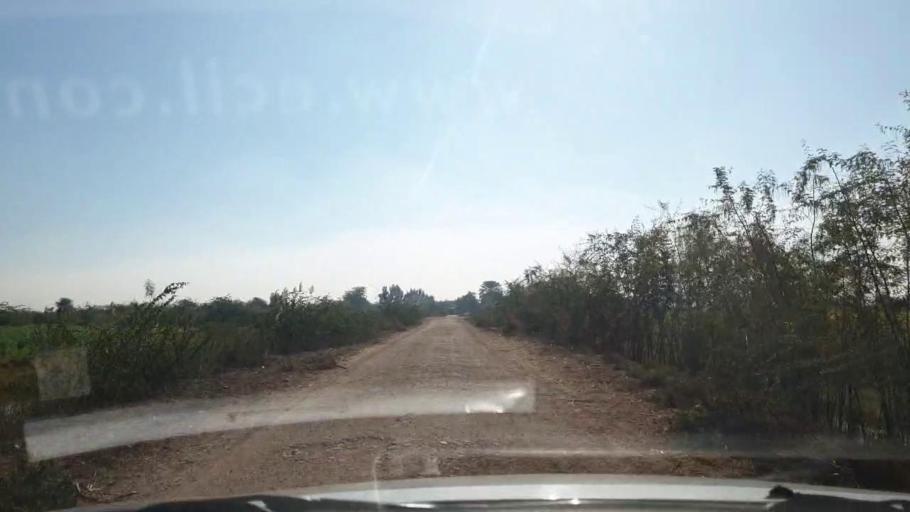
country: PK
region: Sindh
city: Jhol
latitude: 25.8126
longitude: 68.9719
